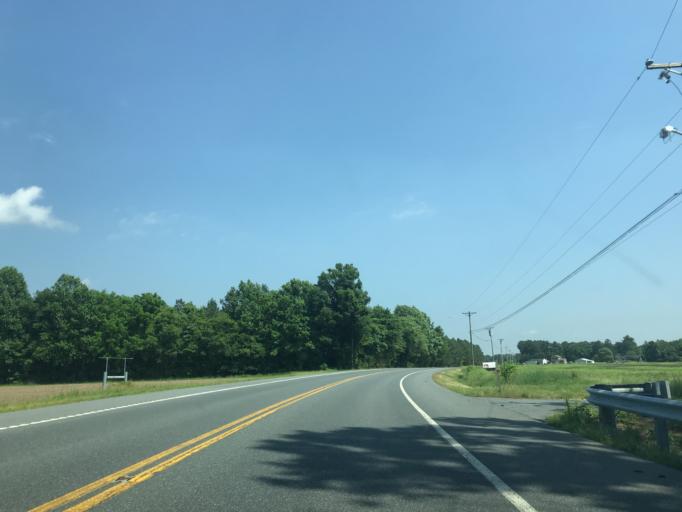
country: US
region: Maryland
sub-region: Dorchester County
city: Hurlock
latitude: 38.5813
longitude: -75.7807
